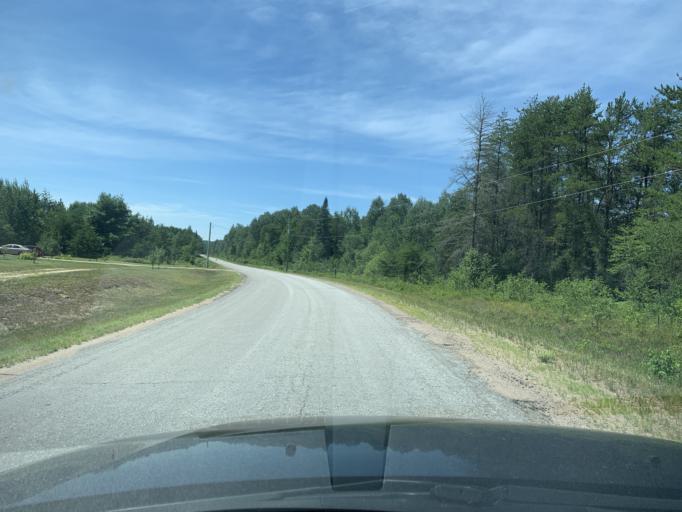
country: CA
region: Ontario
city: Petawawa
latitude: 45.6608
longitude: -77.5917
